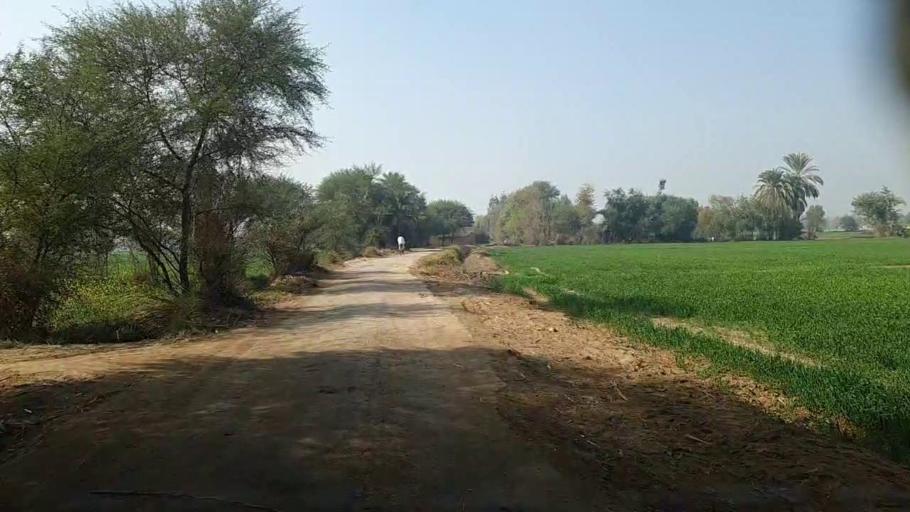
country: PK
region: Sindh
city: Khairpur
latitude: 27.9219
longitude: 69.6636
